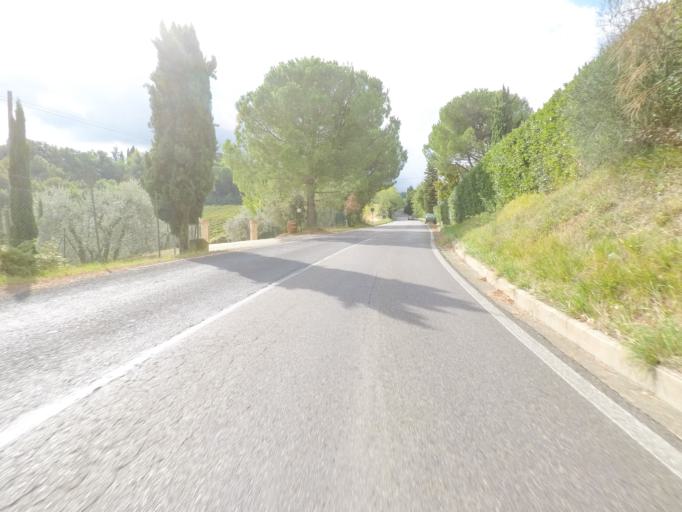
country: IT
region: Tuscany
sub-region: Provincia di Siena
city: Montepulciano
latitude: 43.1140
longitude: 11.7902
